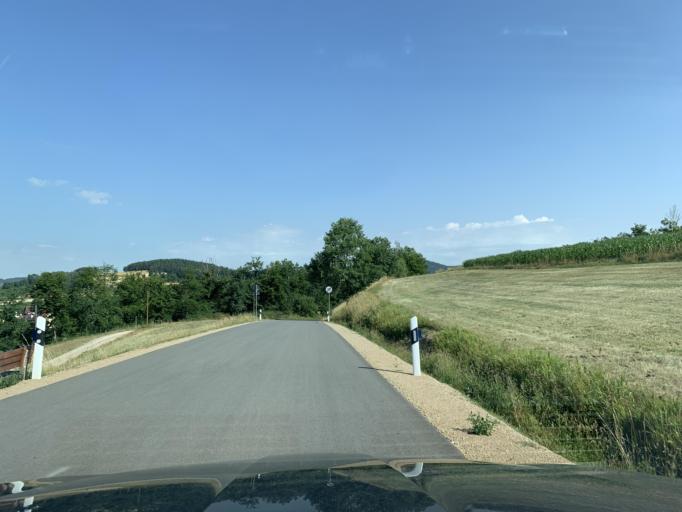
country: DE
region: Bavaria
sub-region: Upper Palatinate
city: Altendorf
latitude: 49.3938
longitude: 12.3110
